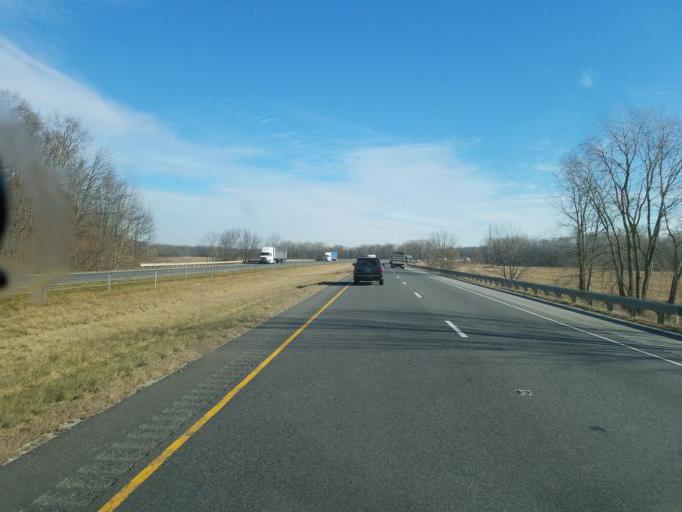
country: US
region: Indiana
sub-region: Henry County
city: Knightstown
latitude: 39.8518
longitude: -85.4855
